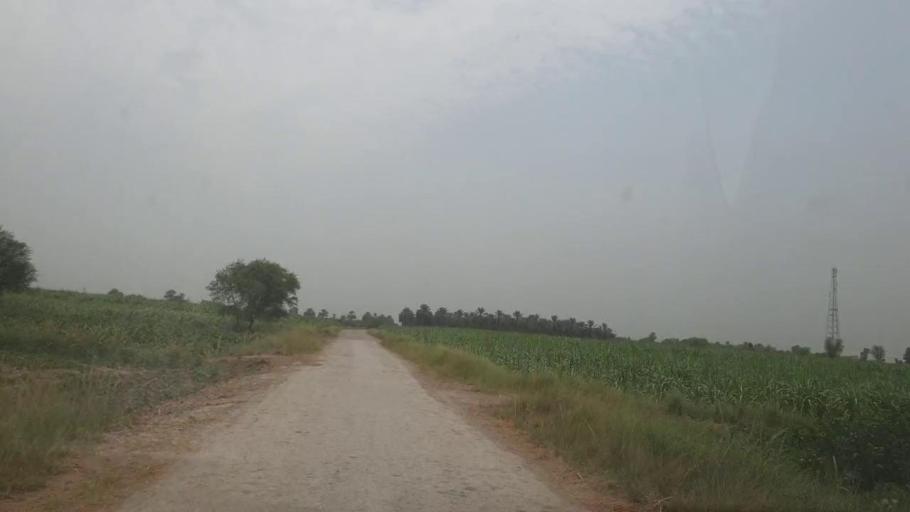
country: PK
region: Sindh
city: Kot Diji
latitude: 27.4362
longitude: 68.6333
